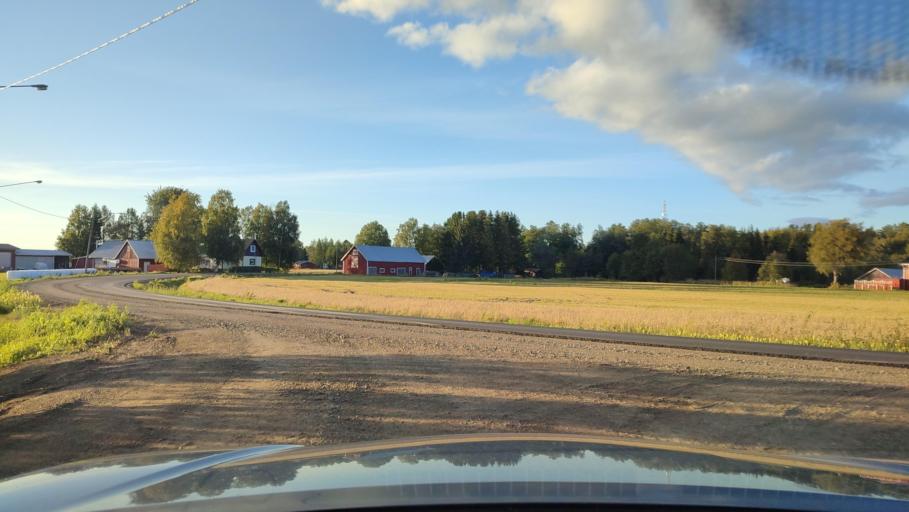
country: FI
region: Southern Ostrobothnia
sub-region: Suupohja
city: Karijoki
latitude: 62.2367
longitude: 21.5697
